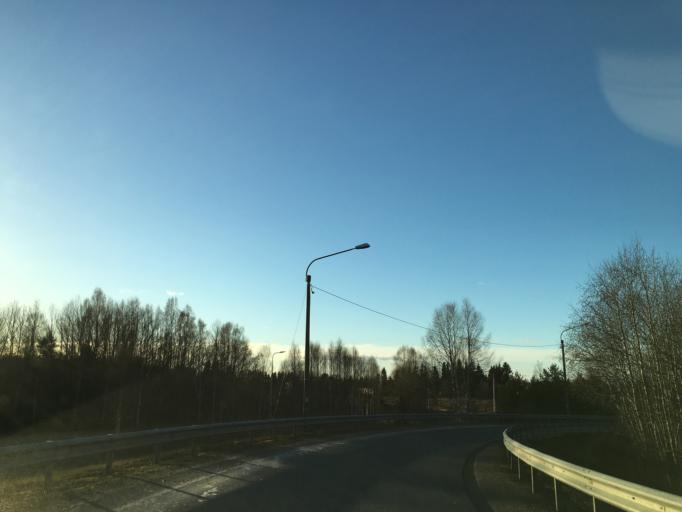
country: EE
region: Harju
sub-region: Saue linn
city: Saue
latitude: 59.3120
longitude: 24.5770
